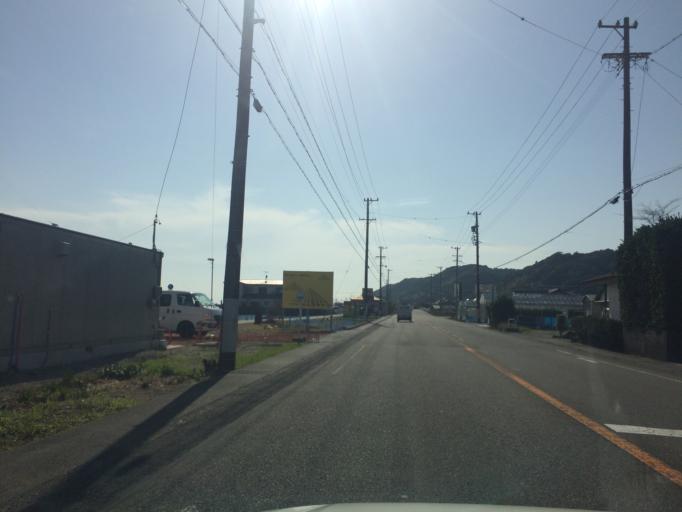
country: JP
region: Shizuoka
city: Sagara
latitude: 34.7135
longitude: 138.2148
